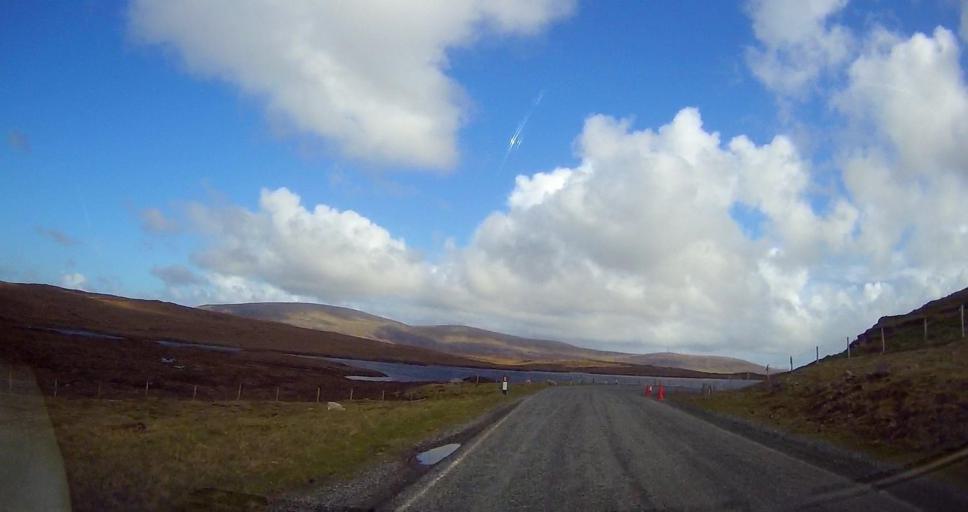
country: GB
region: Scotland
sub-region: Shetland Islands
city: Lerwick
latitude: 60.4846
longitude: -1.4032
